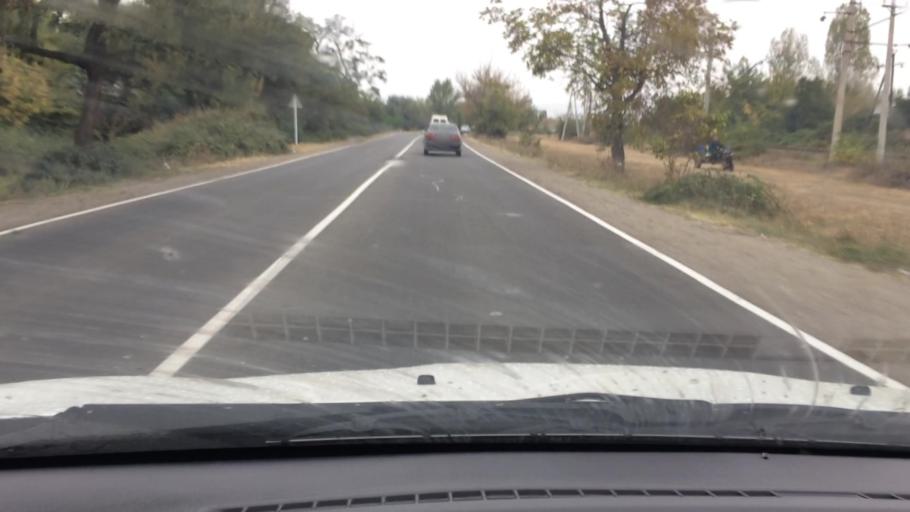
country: GE
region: Kvemo Kartli
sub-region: Marneuli
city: Marneuli
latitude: 41.4146
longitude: 44.8277
